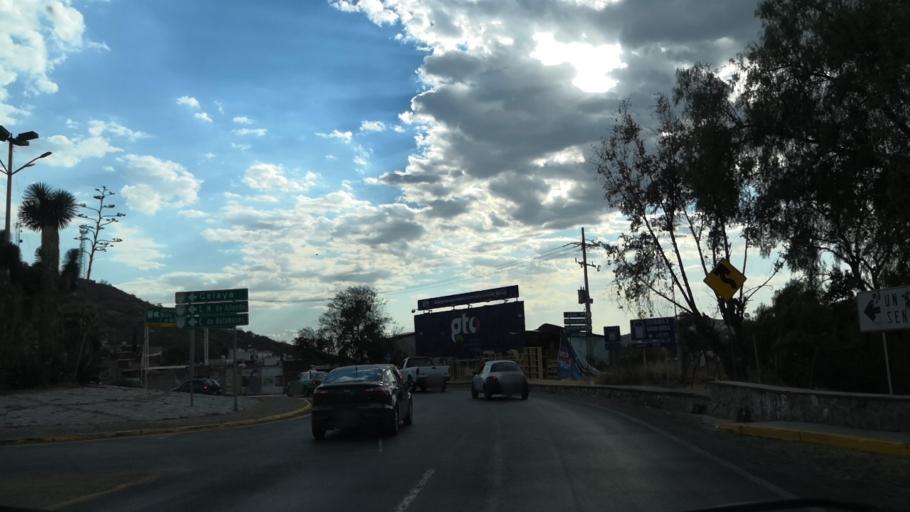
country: MX
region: Guanajuato
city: Marfil
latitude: 20.9979
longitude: -101.2853
